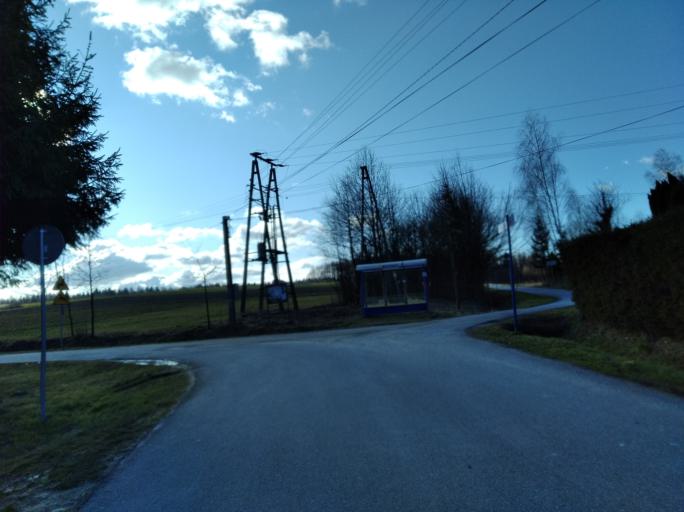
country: PL
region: Subcarpathian Voivodeship
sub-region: Powiat strzyzowski
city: Wisniowa
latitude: 49.9004
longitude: 21.7035
